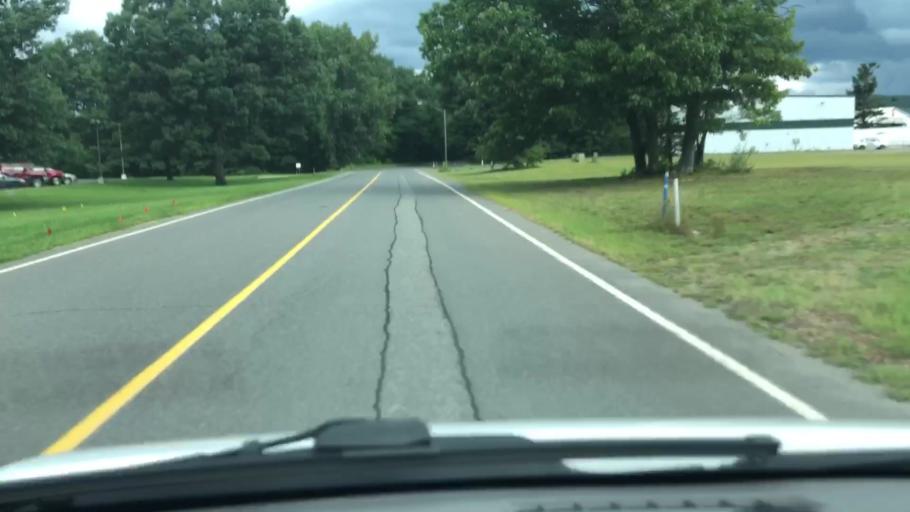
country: US
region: Massachusetts
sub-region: Franklin County
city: Turners Falls
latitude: 42.5926
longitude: -72.5294
